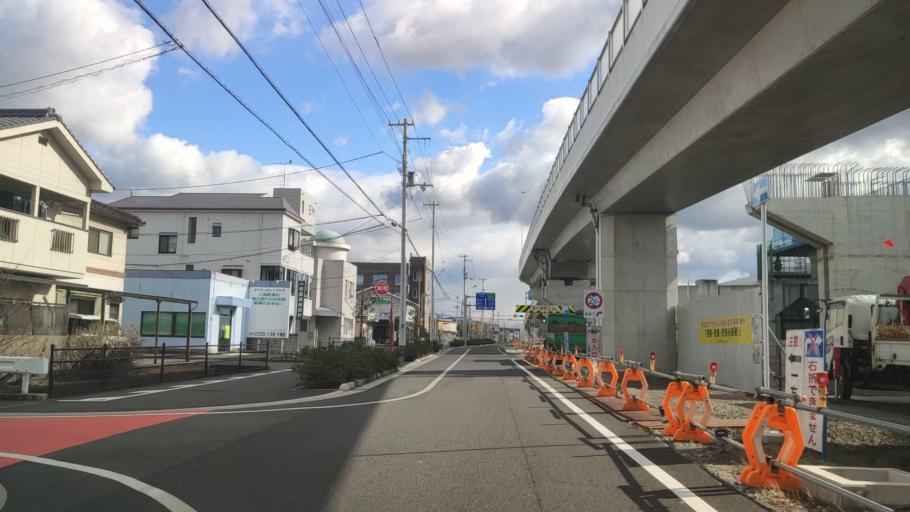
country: JP
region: Ehime
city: Masaki-cho
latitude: 33.8115
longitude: 132.7289
